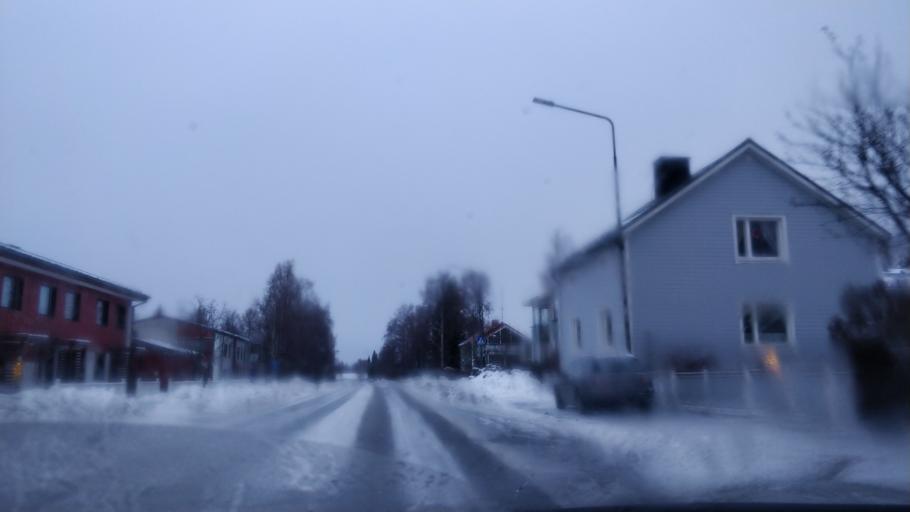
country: FI
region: Lapland
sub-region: Kemi-Tornio
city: Kemi
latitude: 65.7412
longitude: 24.5604
